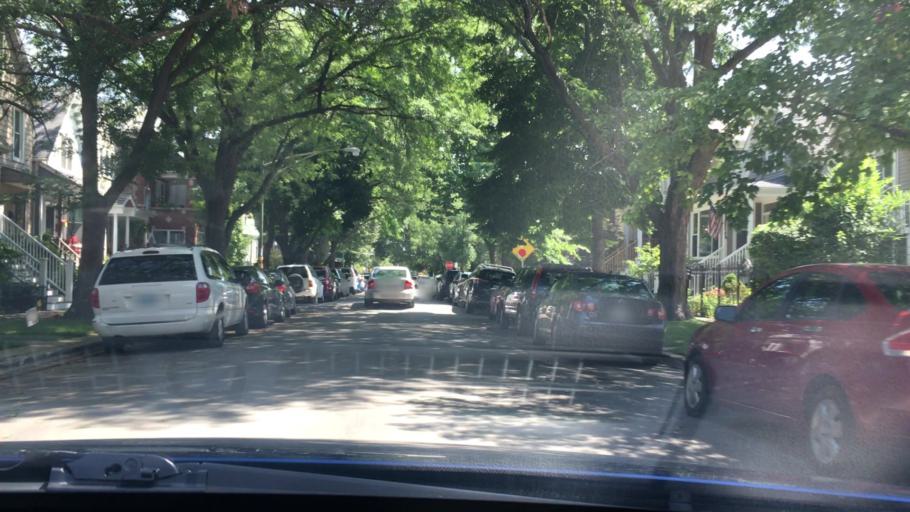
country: US
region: Illinois
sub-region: Cook County
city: Lincolnwood
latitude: 41.9559
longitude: -87.6825
